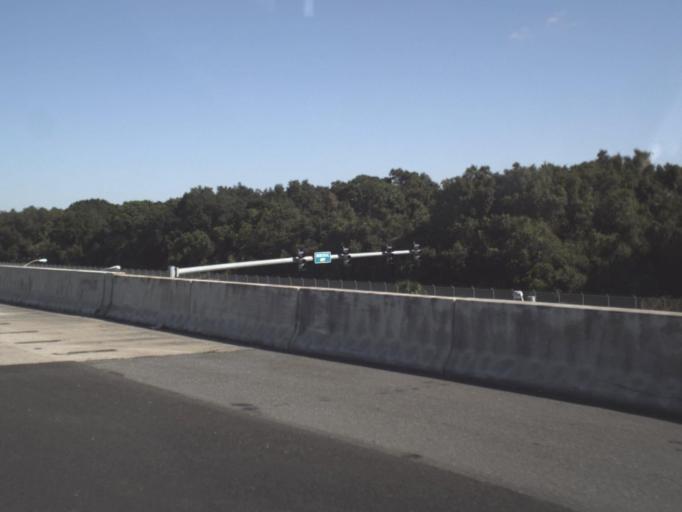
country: US
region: Florida
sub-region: Hillsborough County
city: Town 'n' Country
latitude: 27.9815
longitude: -82.5463
